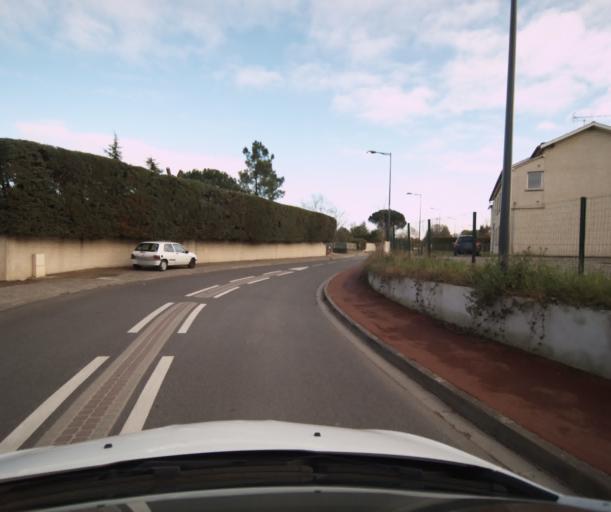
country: FR
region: Midi-Pyrenees
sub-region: Departement de la Haute-Garonne
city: Gratentour
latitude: 43.7281
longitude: 1.4234
